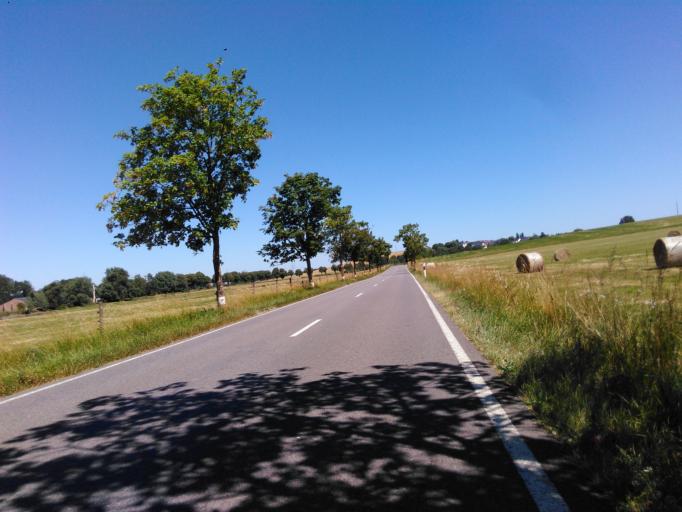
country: LU
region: Luxembourg
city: Bergem
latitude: 49.5113
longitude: 6.0384
